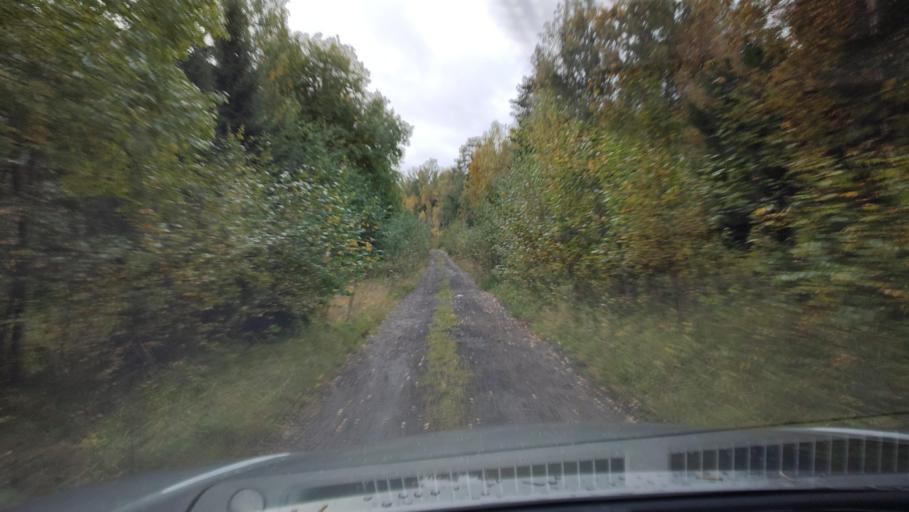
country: FI
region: Ostrobothnia
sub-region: Sydosterbotten
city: Kristinestad
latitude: 62.2715
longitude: 21.4477
